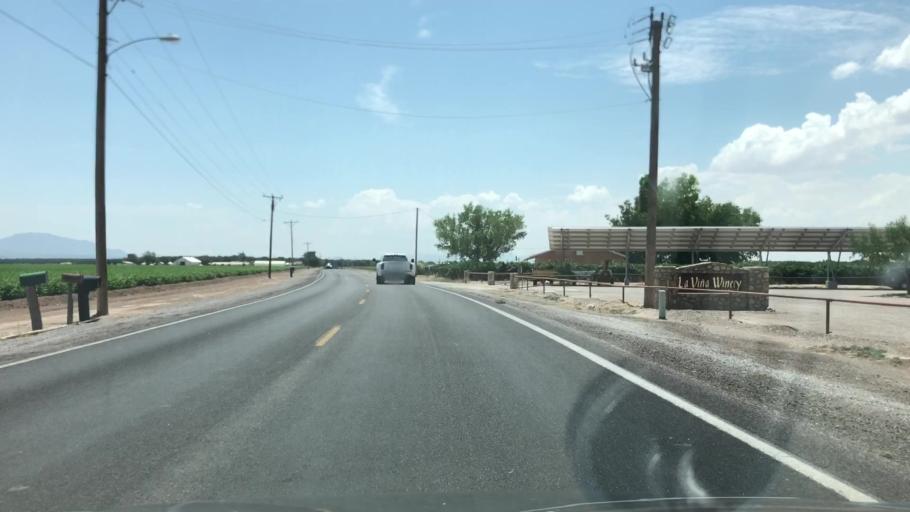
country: US
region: New Mexico
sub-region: Dona Ana County
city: La Union
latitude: 31.9699
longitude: -106.6516
